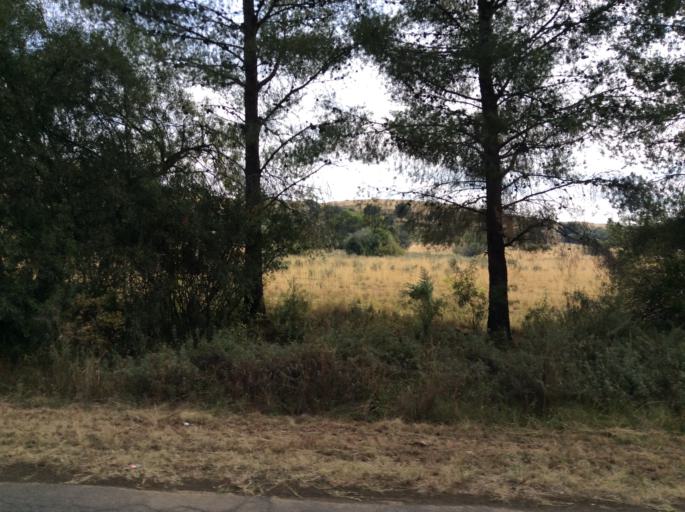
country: ZA
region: Orange Free State
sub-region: Xhariep District Municipality
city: Dewetsdorp
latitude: -29.5729
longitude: 26.6652
